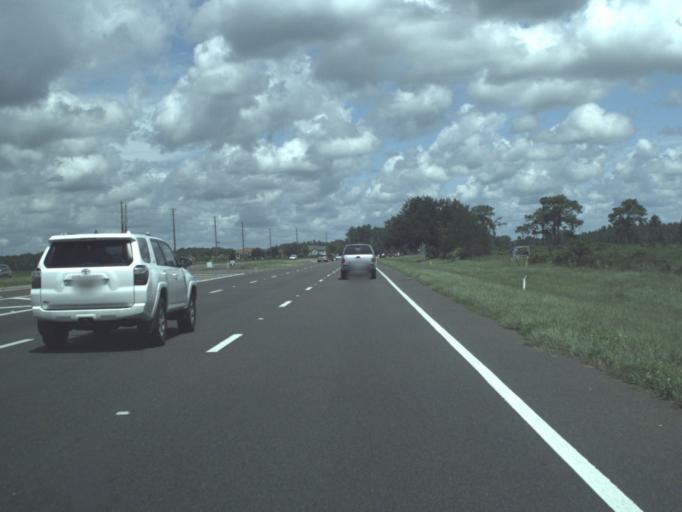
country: US
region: Florida
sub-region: Pasco County
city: Wesley Chapel
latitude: 28.2204
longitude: -82.3532
